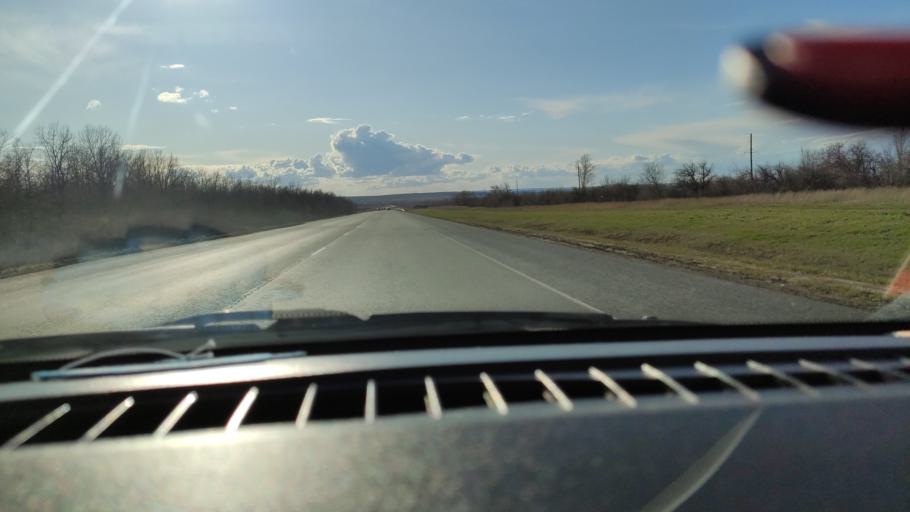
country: RU
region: Saratov
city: Yelshanka
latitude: 51.8274
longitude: 46.2698
